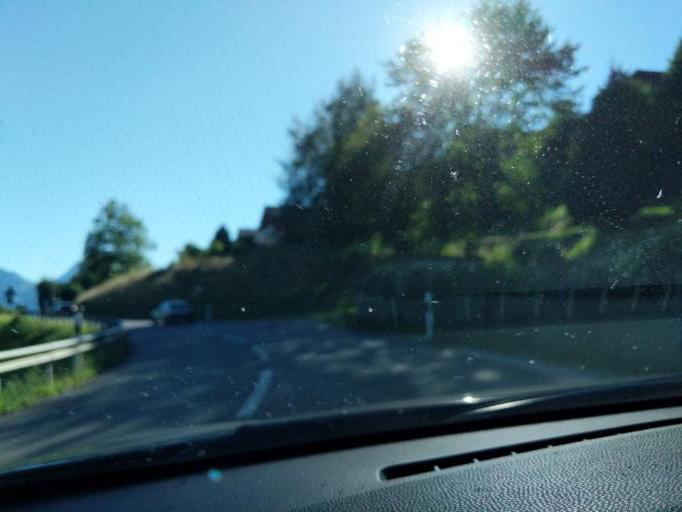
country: CH
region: Fribourg
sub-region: Gruyere District
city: Broc
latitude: 46.6151
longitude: 7.1314
